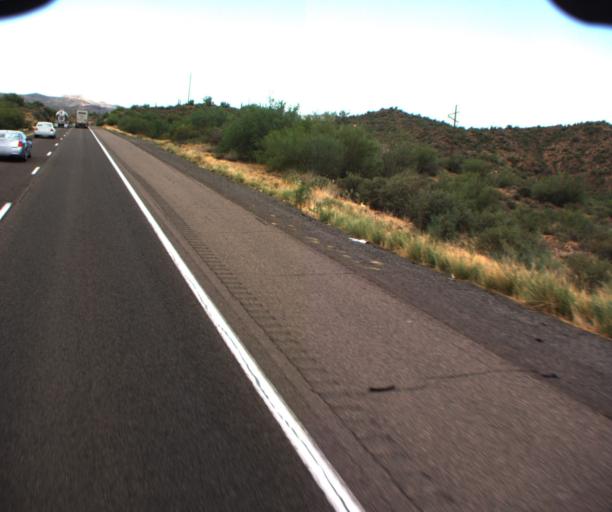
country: US
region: Arizona
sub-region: Yavapai County
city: Black Canyon City
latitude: 34.0266
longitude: -112.1473
